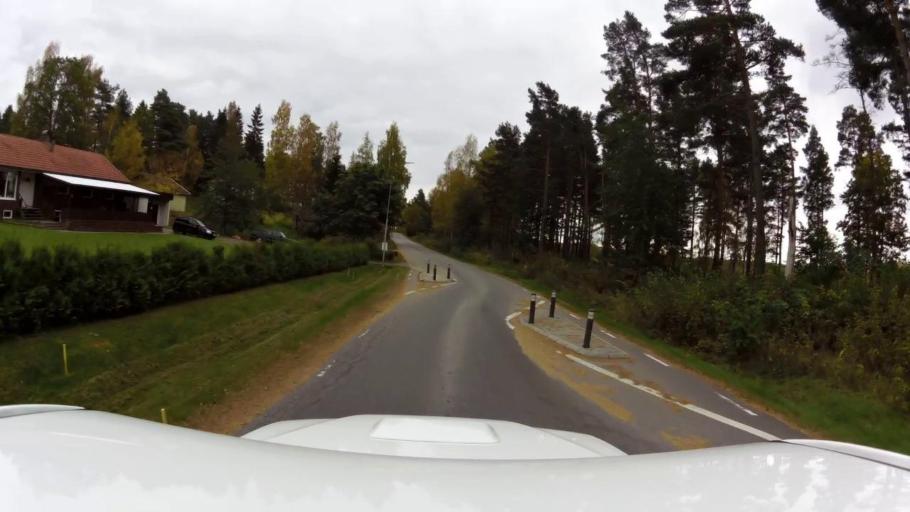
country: SE
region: OEstergoetland
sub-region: Linkopings Kommun
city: Ljungsbro
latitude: 58.5202
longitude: 15.4913
